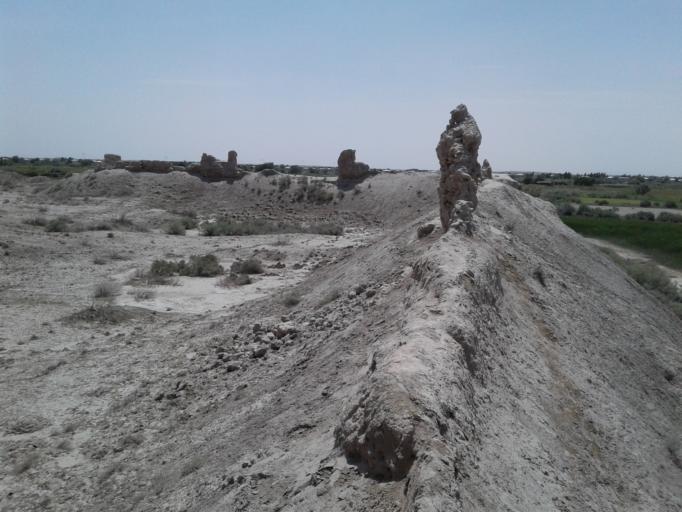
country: TM
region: Dasoguz
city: Tagta
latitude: 41.5419
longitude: 59.9980
